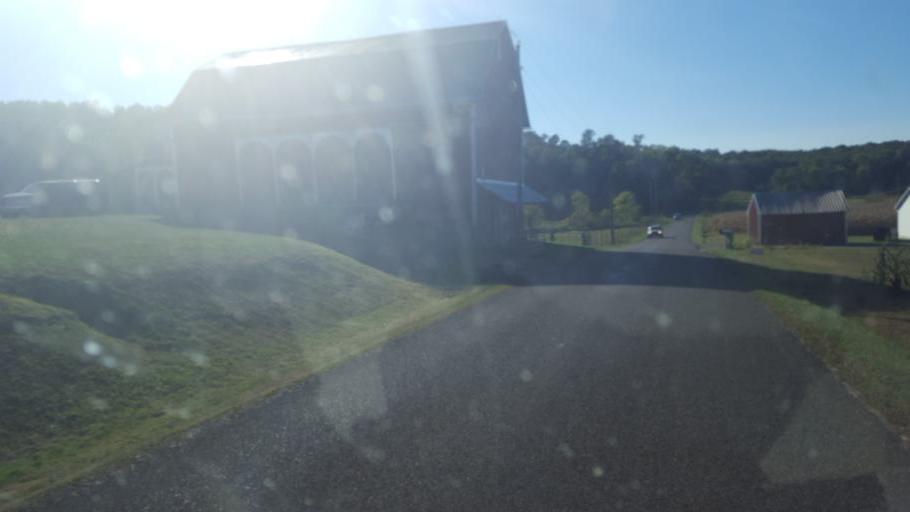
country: US
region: Ohio
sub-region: Richland County
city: Lexington
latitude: 40.6510
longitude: -82.5564
